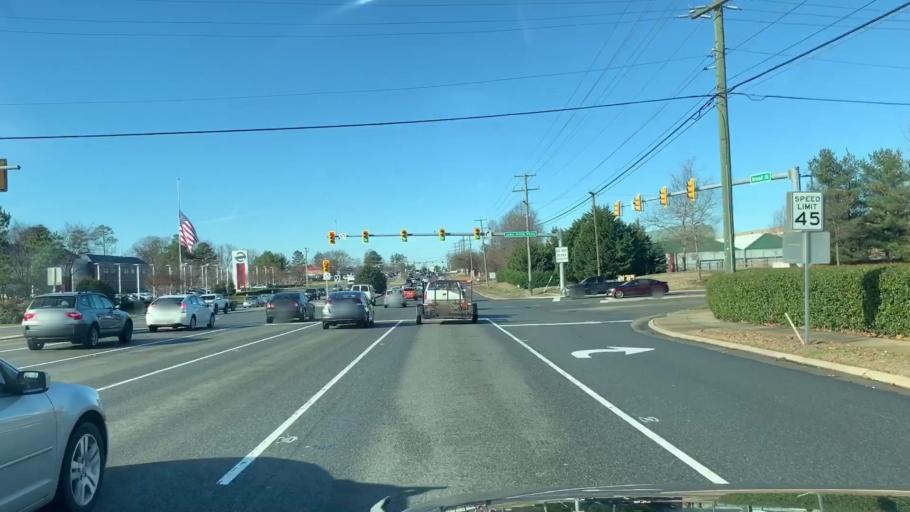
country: US
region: Virginia
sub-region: Henrico County
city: Short Pump
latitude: 37.6505
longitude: -77.6069
